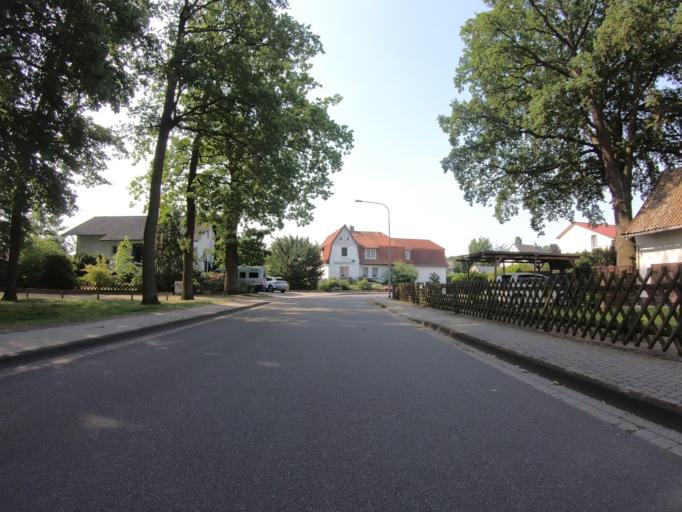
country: DE
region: Lower Saxony
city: Gifhorn
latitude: 52.4849
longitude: 10.5342
